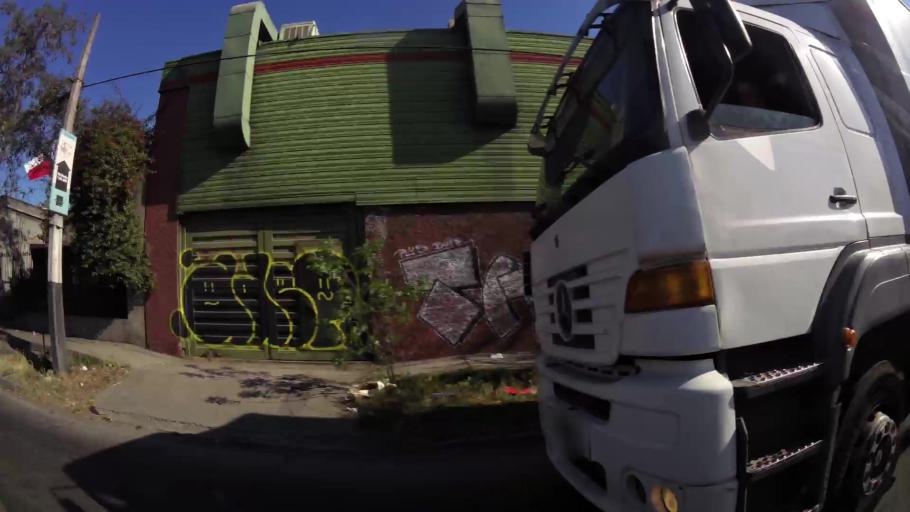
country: CL
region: Santiago Metropolitan
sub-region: Provincia de Santiago
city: Santiago
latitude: -33.4793
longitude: -70.6518
